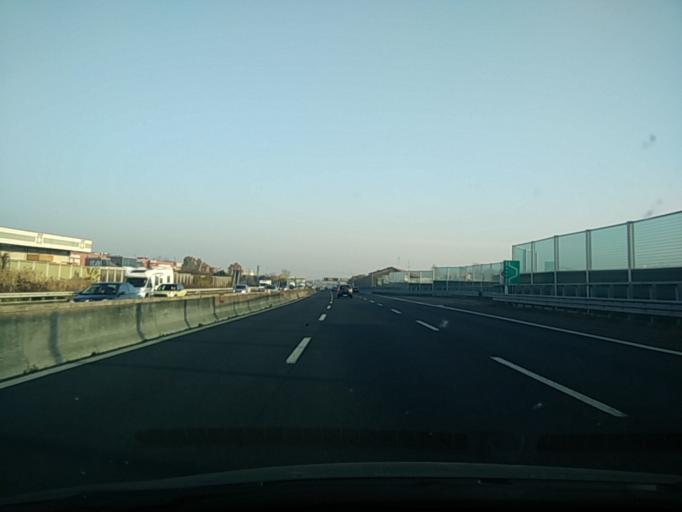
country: IT
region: Lombardy
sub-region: Provincia di Brescia
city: Villa Pedergnano
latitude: 45.5796
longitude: 9.9933
